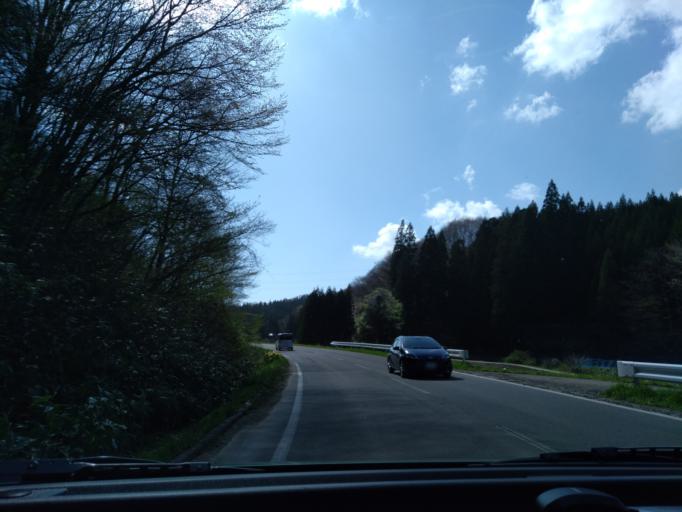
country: JP
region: Akita
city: Akita
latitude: 39.6958
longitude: 140.2365
